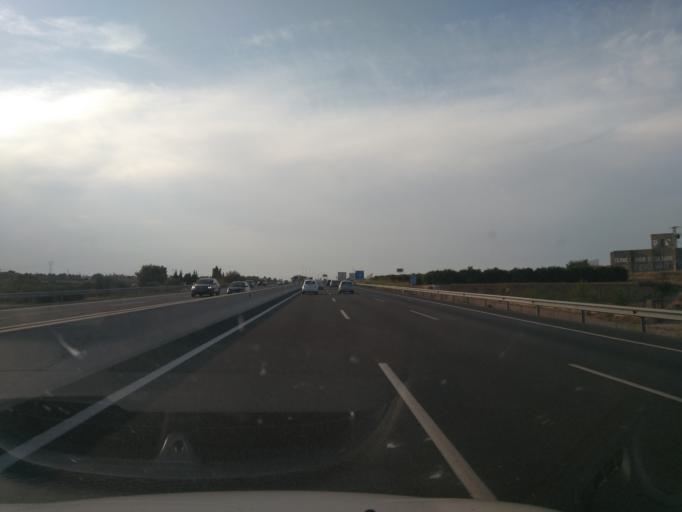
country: ES
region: Valencia
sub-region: Provincia de Valencia
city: Picassent
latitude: 39.3948
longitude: -0.4866
